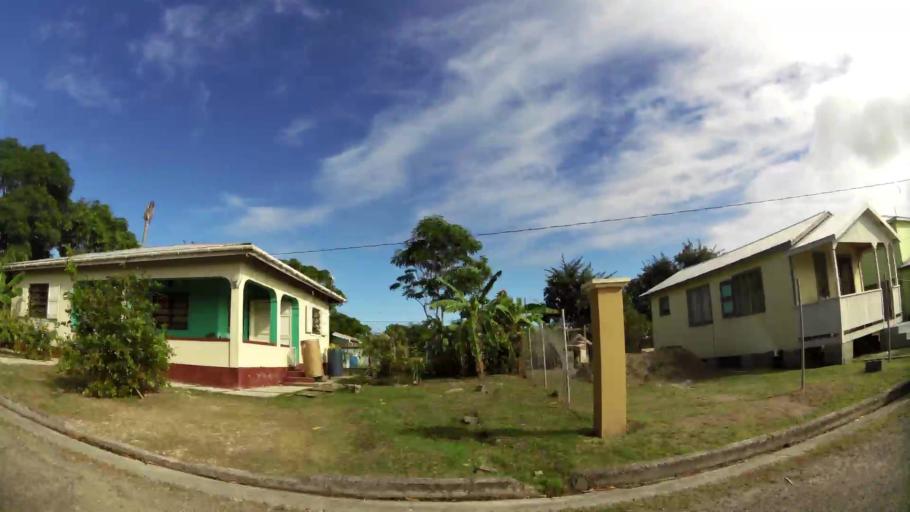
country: AG
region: Saint Peter
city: All Saints
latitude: 17.0531
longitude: -61.8004
